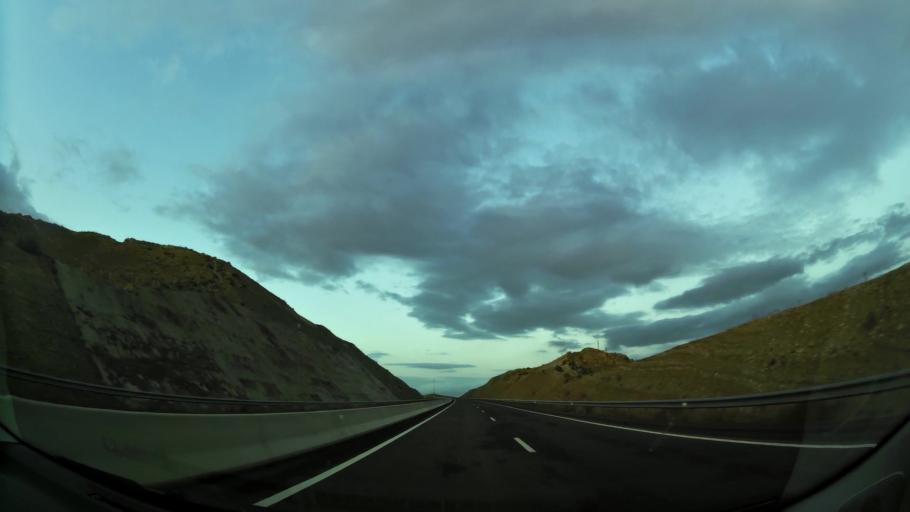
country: MA
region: Oriental
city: El Aioun
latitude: 34.5942
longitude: -2.6644
